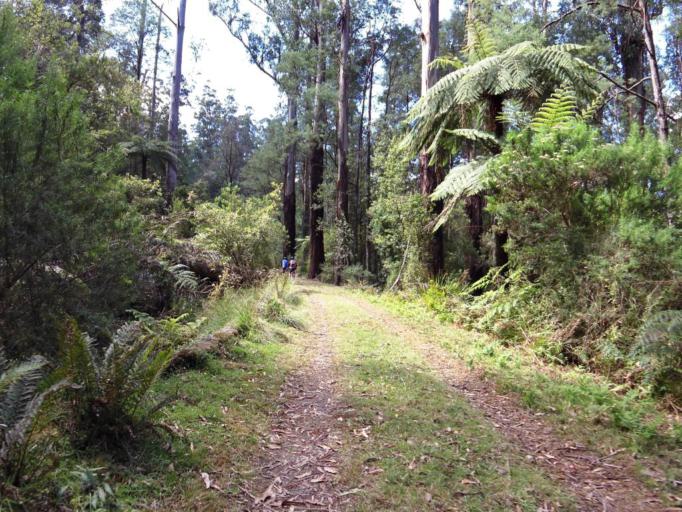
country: AU
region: Victoria
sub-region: Yarra Ranges
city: Millgrove
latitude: -37.7034
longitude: 145.7824
